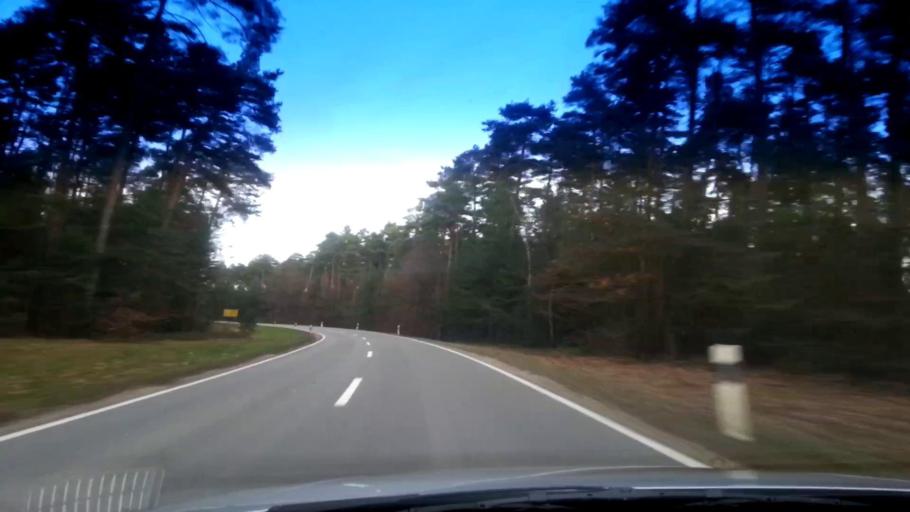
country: DE
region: Bavaria
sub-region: Upper Franconia
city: Strullendorf
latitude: 49.8555
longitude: 10.9728
